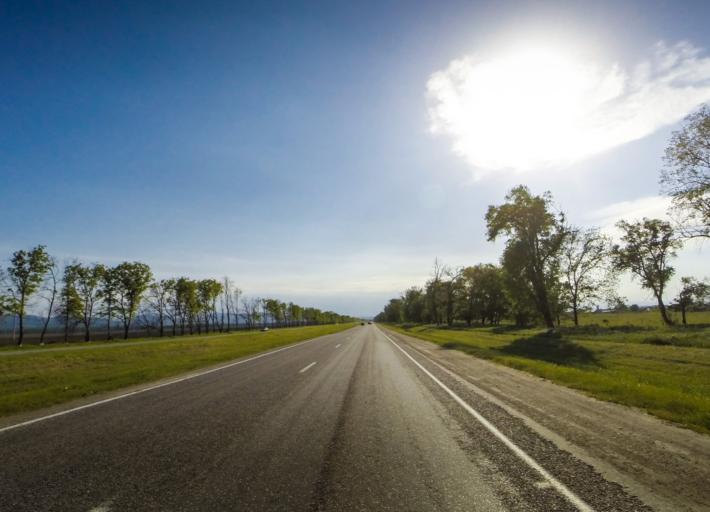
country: RU
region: Kabardino-Balkariya
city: Nartan
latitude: 43.5006
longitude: 43.7144
